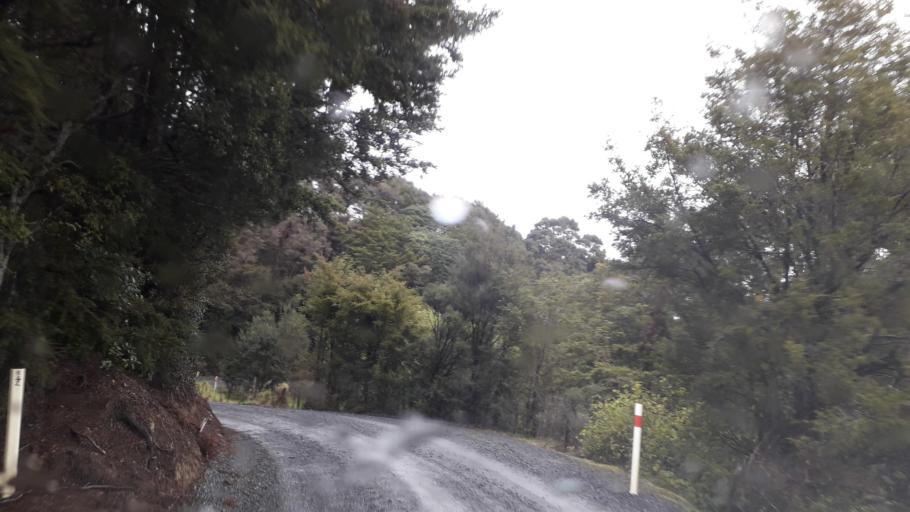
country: NZ
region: Northland
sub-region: Far North District
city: Waimate North
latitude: -35.1324
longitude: 173.7183
